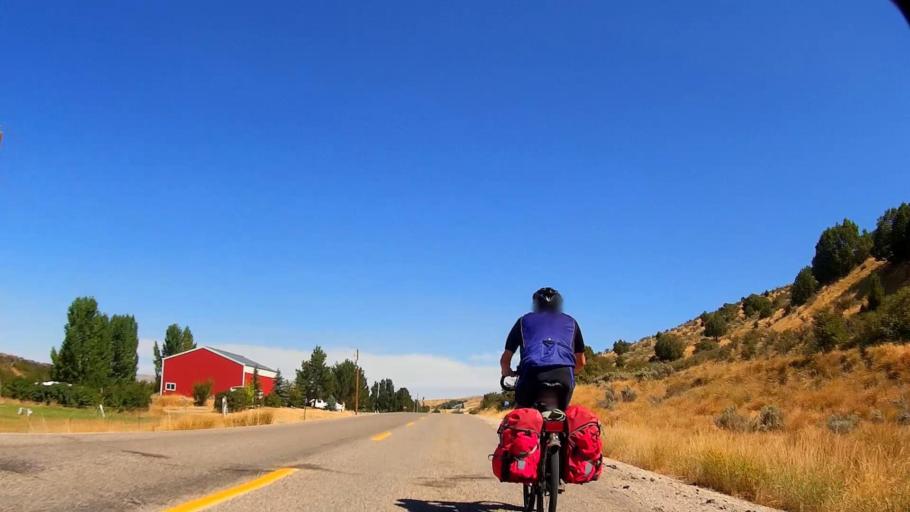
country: US
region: Idaho
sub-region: Bannock County
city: Pocatello
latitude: 42.7161
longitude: -112.2078
